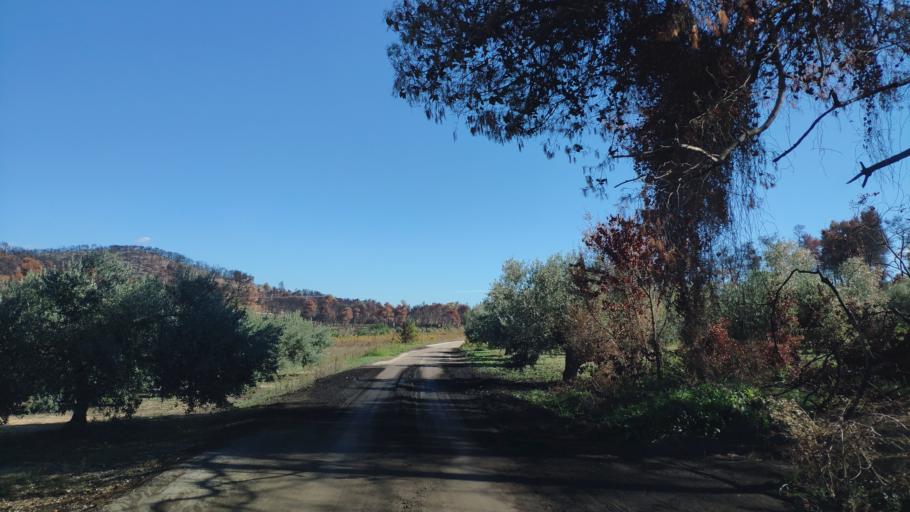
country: GR
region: Peloponnese
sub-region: Nomos Korinthias
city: Athikia
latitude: 37.8445
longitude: 22.9422
